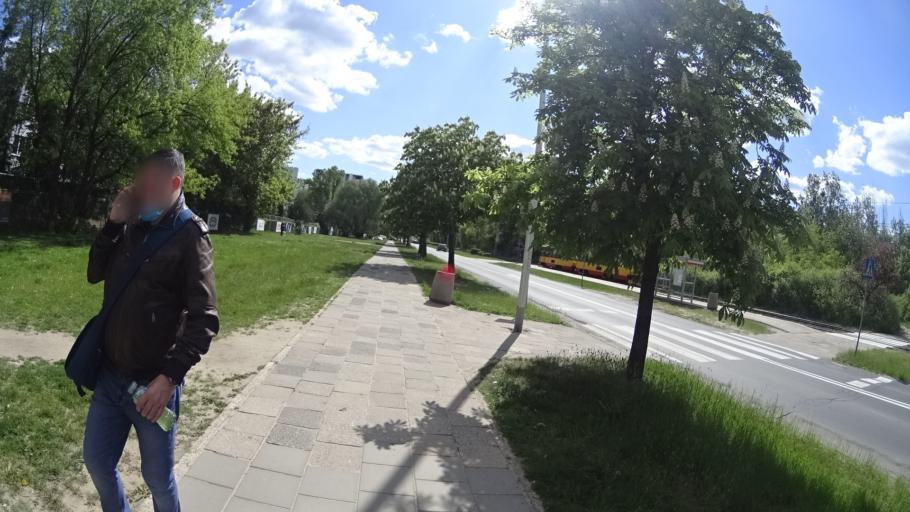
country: PL
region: Masovian Voivodeship
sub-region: Warszawa
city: Bielany
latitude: 52.2848
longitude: 20.9234
